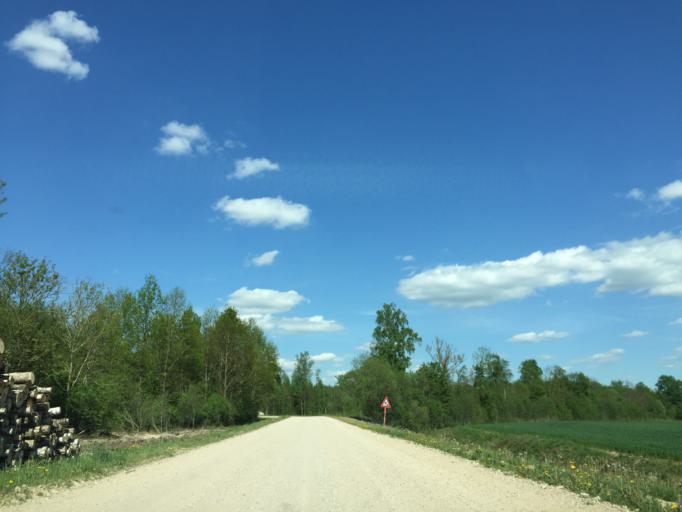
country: LV
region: Rundales
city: Pilsrundale
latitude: 56.3487
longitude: 23.9546
